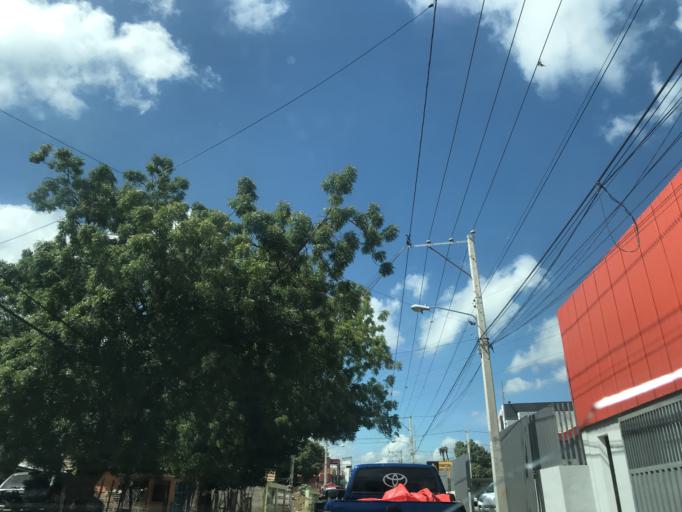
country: DO
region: Santiago
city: Palmar Arriba
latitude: 19.4909
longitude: -70.7413
